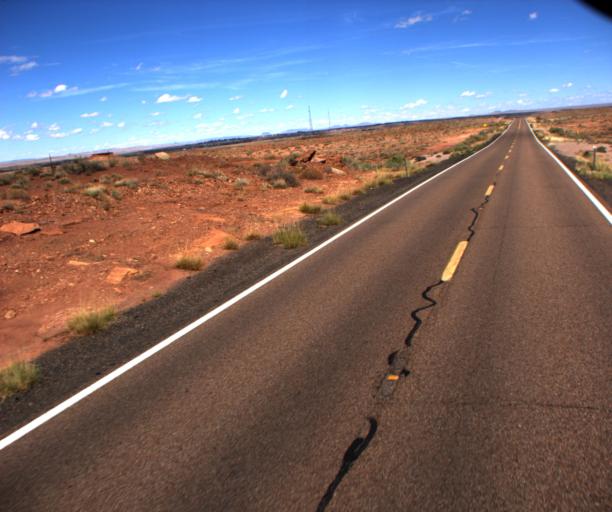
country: US
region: Arizona
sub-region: Navajo County
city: Holbrook
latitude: 34.8544
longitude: -110.1711
